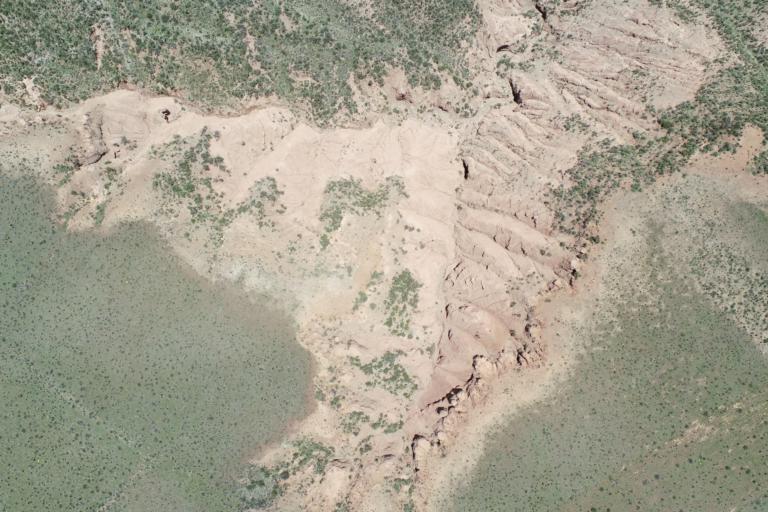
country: BO
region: La Paz
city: Curahuara de Carangas
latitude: -17.3079
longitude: -68.5002
